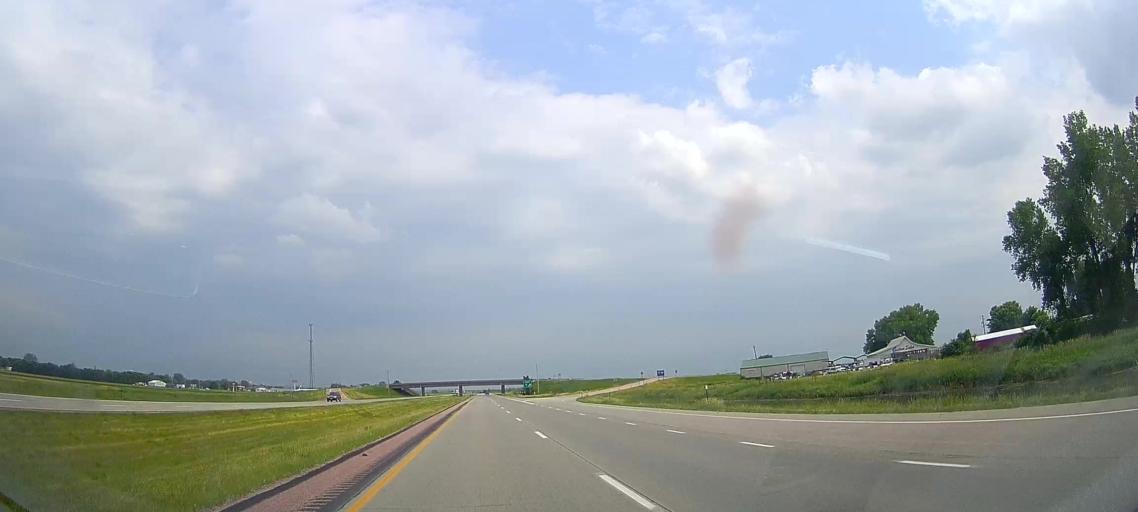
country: US
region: South Dakota
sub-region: Union County
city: North Sioux City
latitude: 42.6073
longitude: -96.5795
